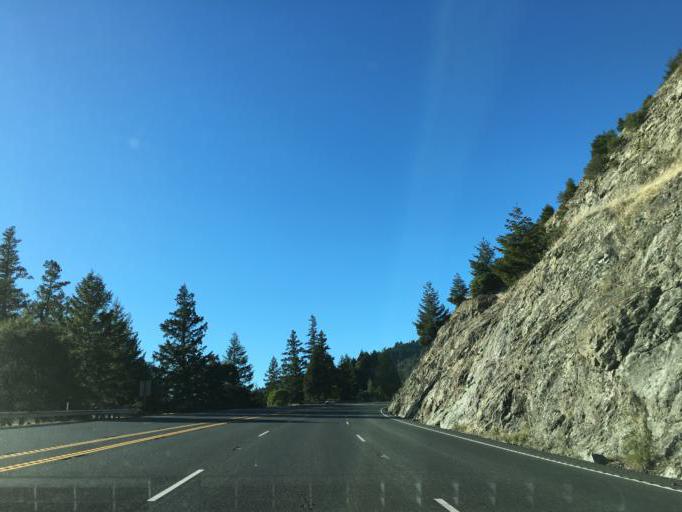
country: US
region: California
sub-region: Mendocino County
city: Laytonville
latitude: 39.8329
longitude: -123.6248
